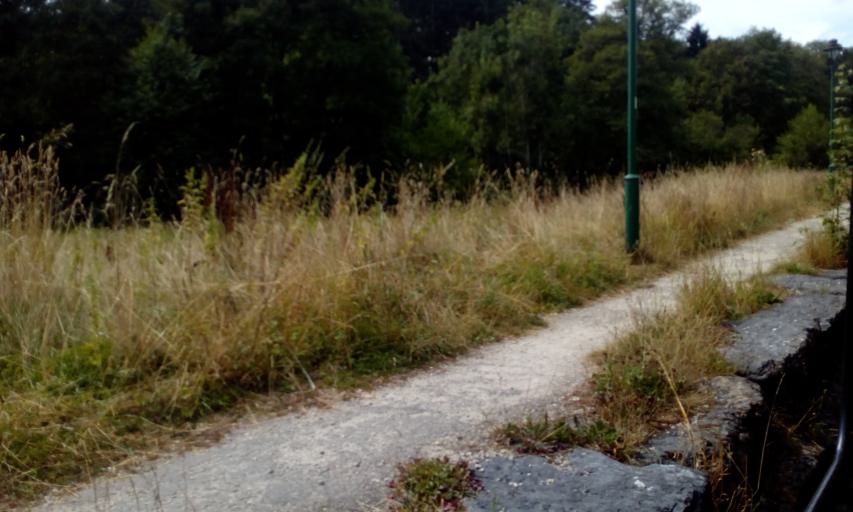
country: BE
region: Wallonia
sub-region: Province du Luxembourg
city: Tellin
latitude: 50.1228
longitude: 5.1875
